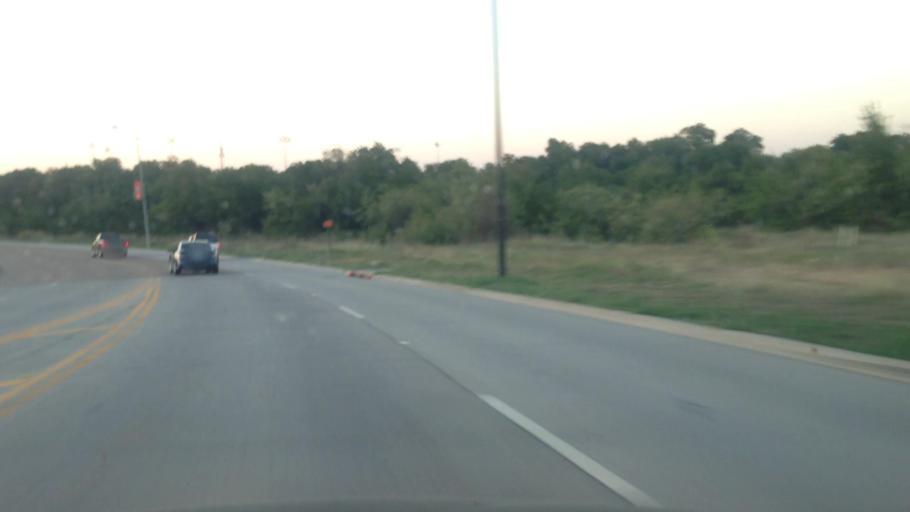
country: US
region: Texas
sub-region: Tarrant County
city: Watauga
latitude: 32.8436
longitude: -97.2752
